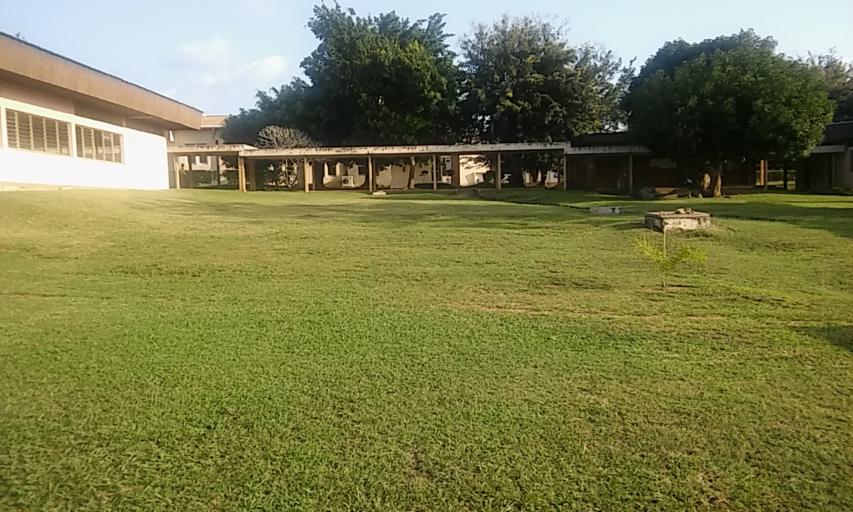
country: CI
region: Vallee du Bandama
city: Bouake
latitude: 7.6878
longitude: -5.0668
